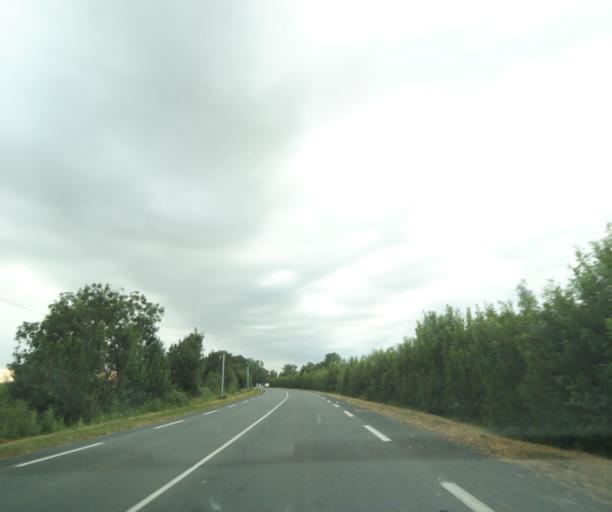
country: FR
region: Pays de la Loire
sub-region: Departement de la Vendee
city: Chaille-les-Marais
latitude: 46.4111
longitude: -1.0398
